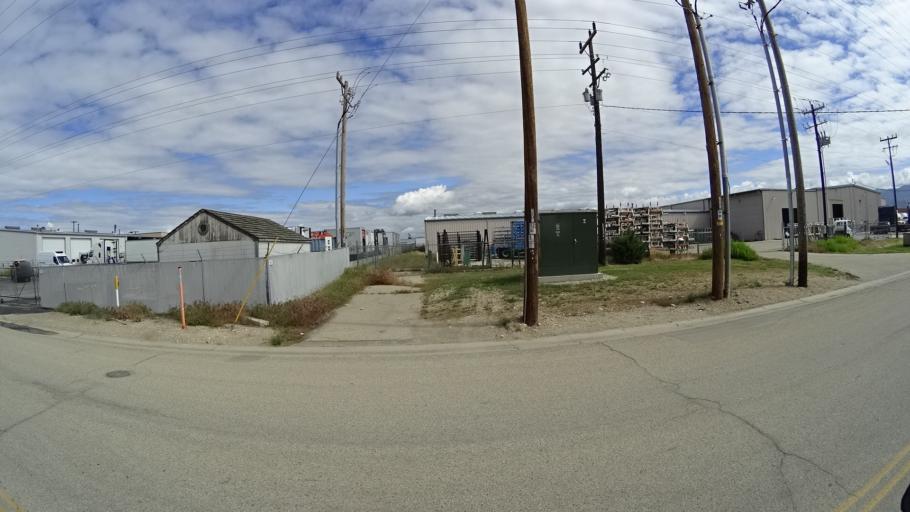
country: US
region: Idaho
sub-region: Ada County
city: Boise
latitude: 43.5604
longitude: -116.1972
